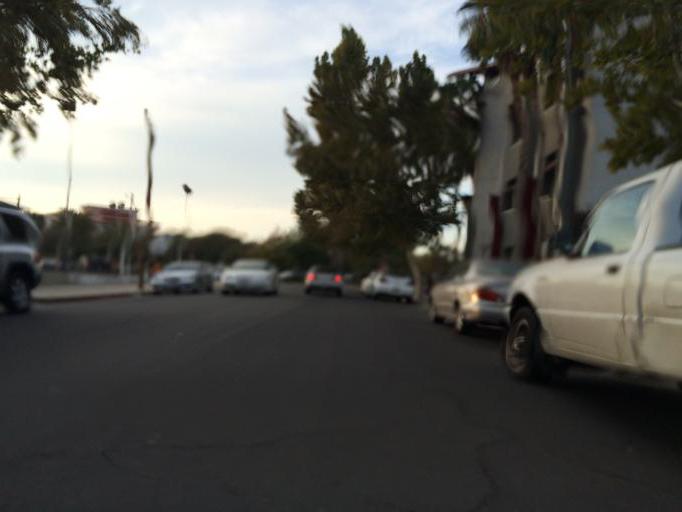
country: US
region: California
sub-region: Fresno County
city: Fresno
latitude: 36.7440
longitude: -119.7794
